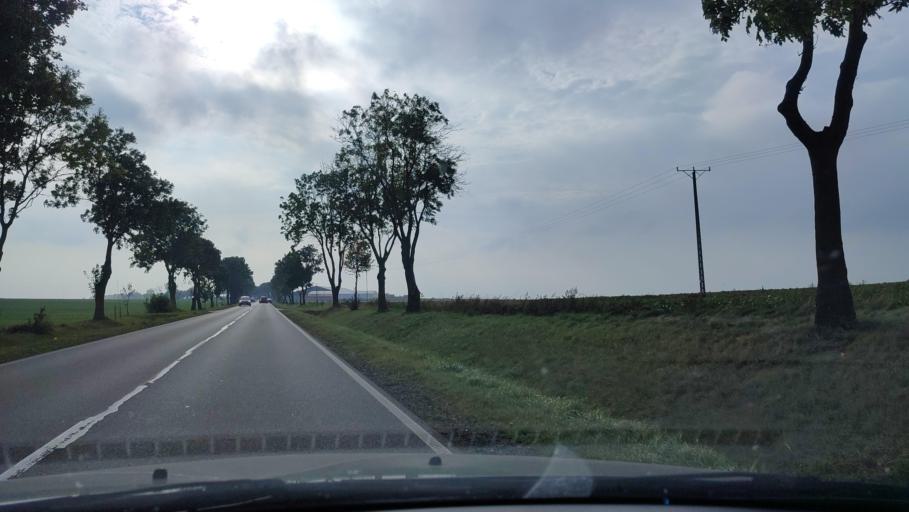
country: PL
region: Warmian-Masurian Voivodeship
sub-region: Powiat nidzicki
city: Kozlowo
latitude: 53.3315
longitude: 20.3238
